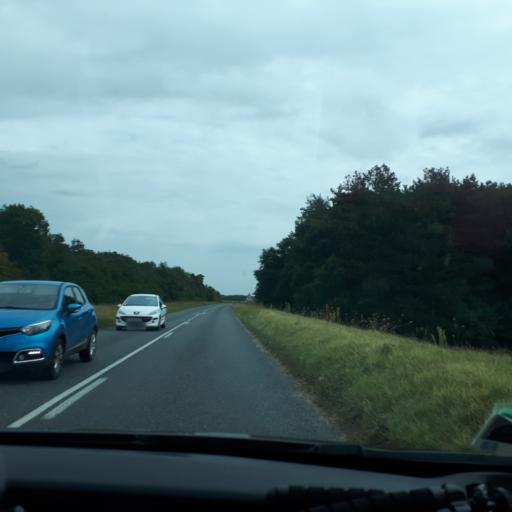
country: FR
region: Centre
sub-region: Departement du Loiret
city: Sully-sur-Loire
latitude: 47.7753
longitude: 2.3950
